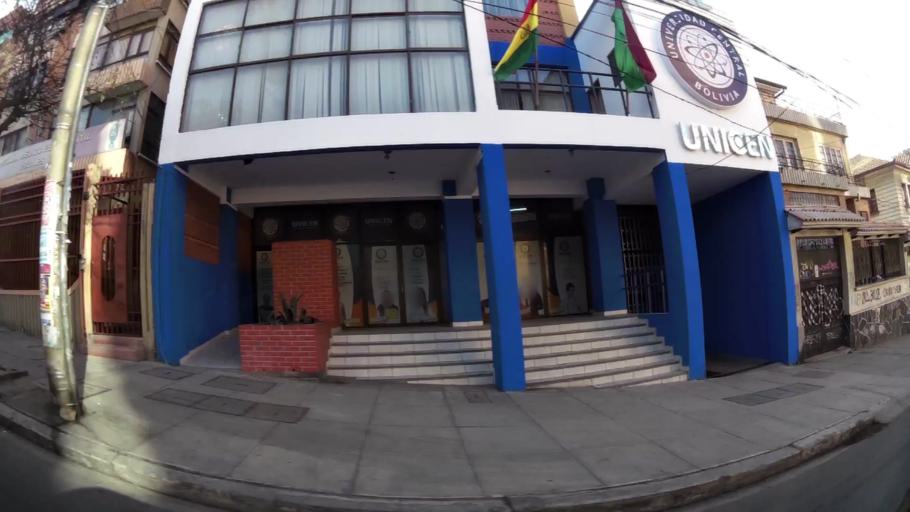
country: BO
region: La Paz
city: La Paz
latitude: -16.4981
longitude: -68.1187
